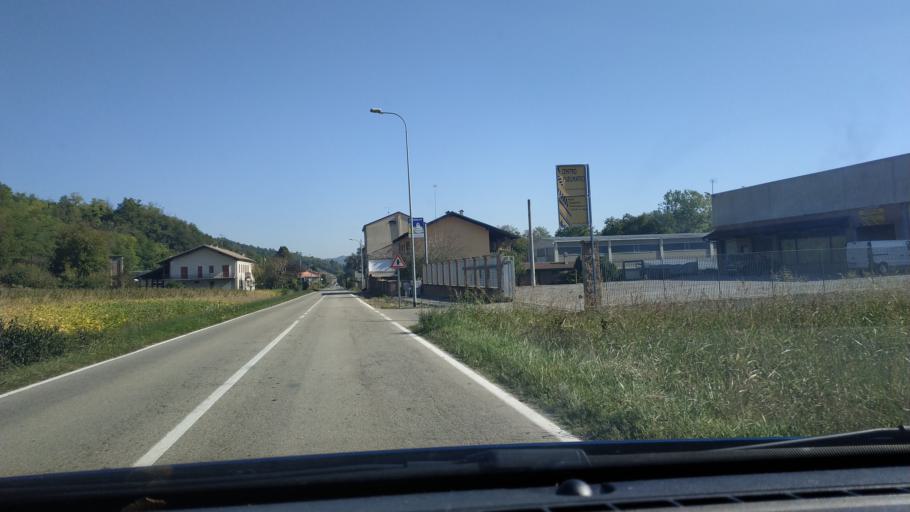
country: IT
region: Piedmont
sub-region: Provincia di Alessandria
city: Cerrina
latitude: 45.1029
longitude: 8.1963
